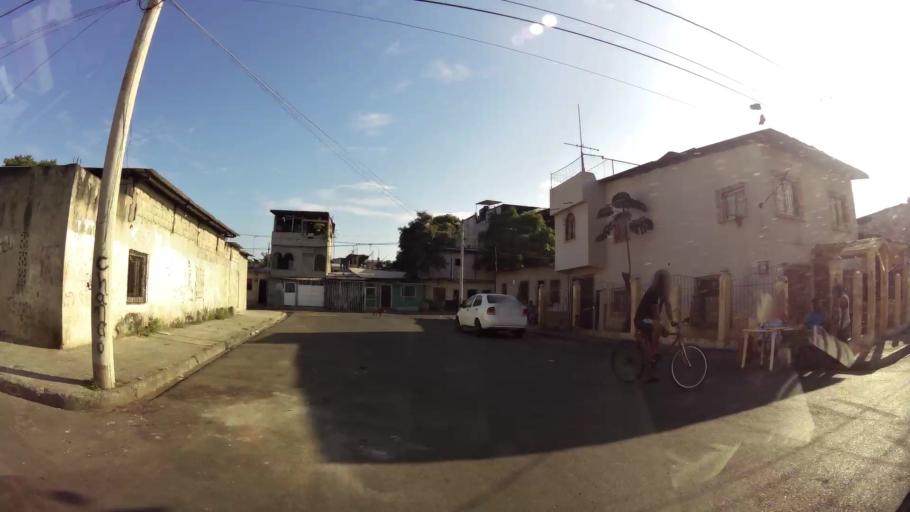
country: EC
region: Guayas
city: Guayaquil
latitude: -2.2205
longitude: -79.9178
